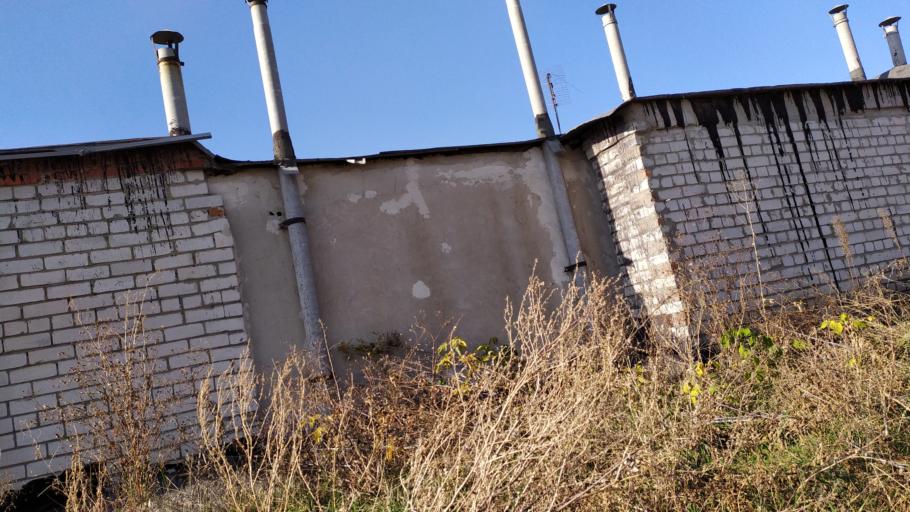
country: RU
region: Kursk
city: Kursk
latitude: 51.6506
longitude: 36.1526
